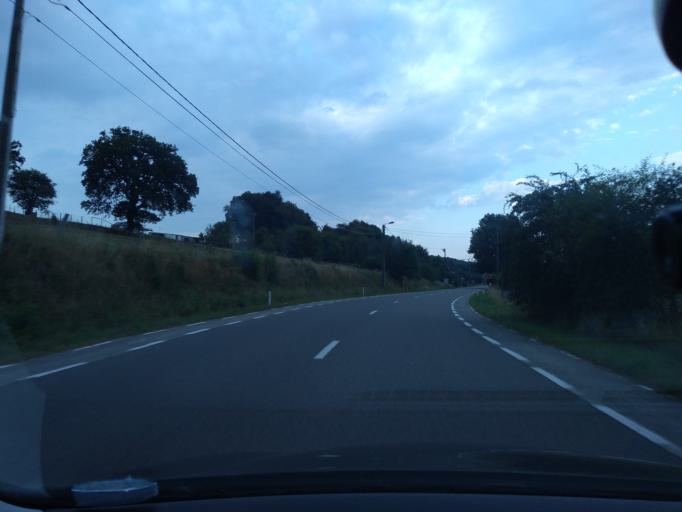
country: BE
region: Wallonia
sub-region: Province du Luxembourg
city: Saint-Hubert
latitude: 50.0242
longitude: 5.3525
